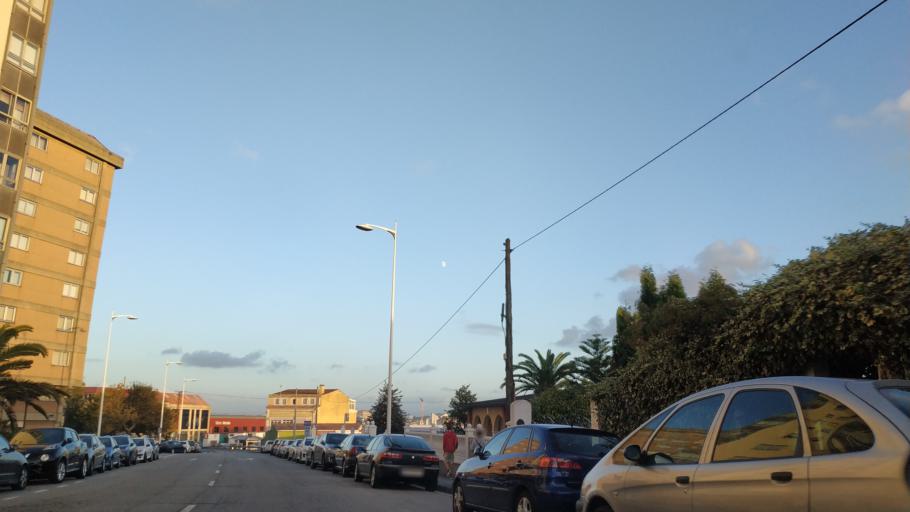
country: ES
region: Galicia
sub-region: Provincia da Coruna
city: A Coruna
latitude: 43.3582
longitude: -8.4247
